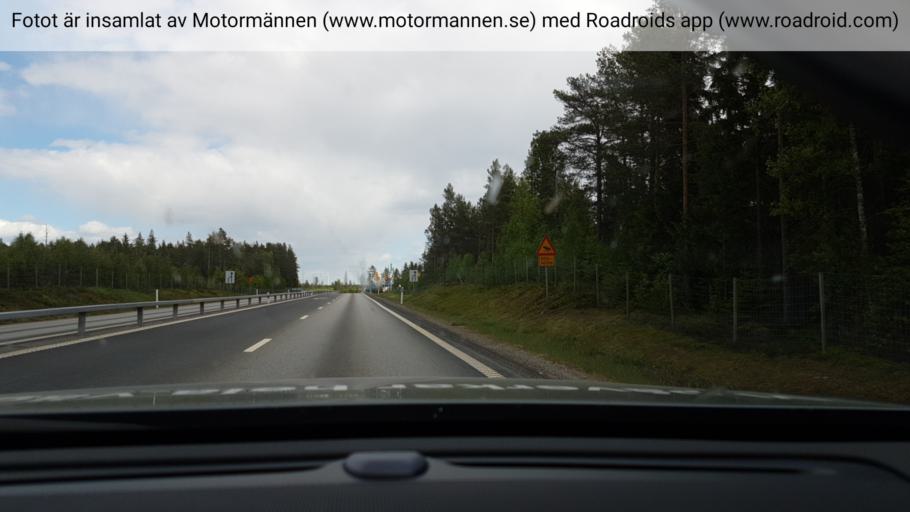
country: SE
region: Vaesterbotten
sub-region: Umea Kommun
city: Hoernefors
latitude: 63.6289
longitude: 19.8694
